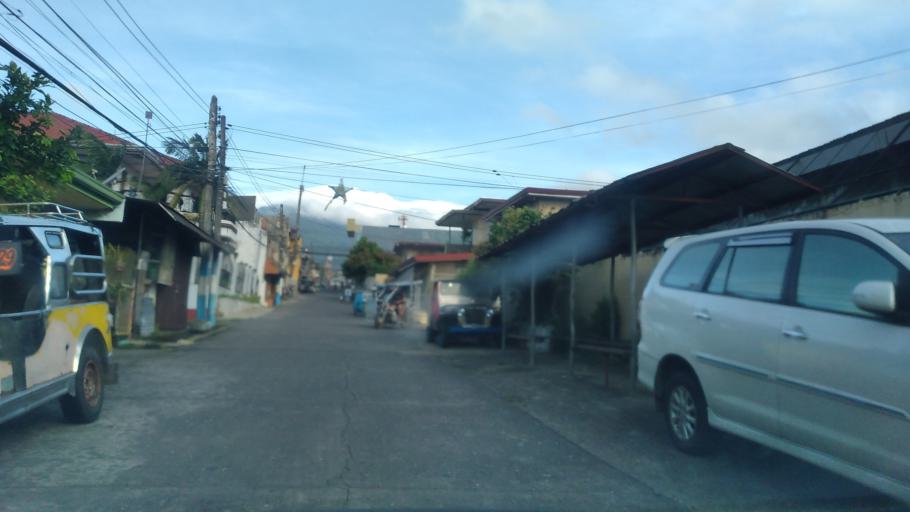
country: PH
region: Calabarzon
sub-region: Province of Quezon
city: Sariaya
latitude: 13.9624
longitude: 121.5265
